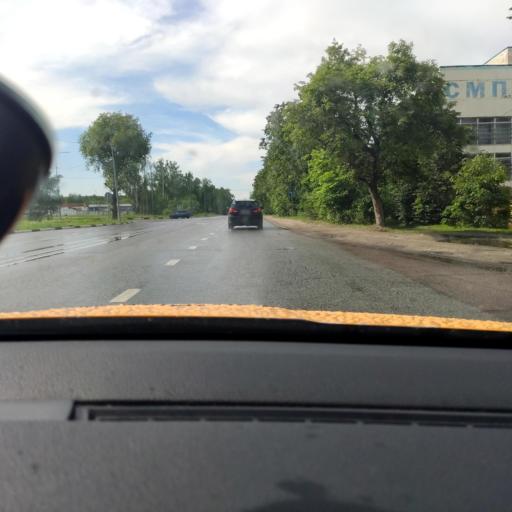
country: RU
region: Moskovskaya
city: Stupino
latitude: 54.9164
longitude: 38.0636
